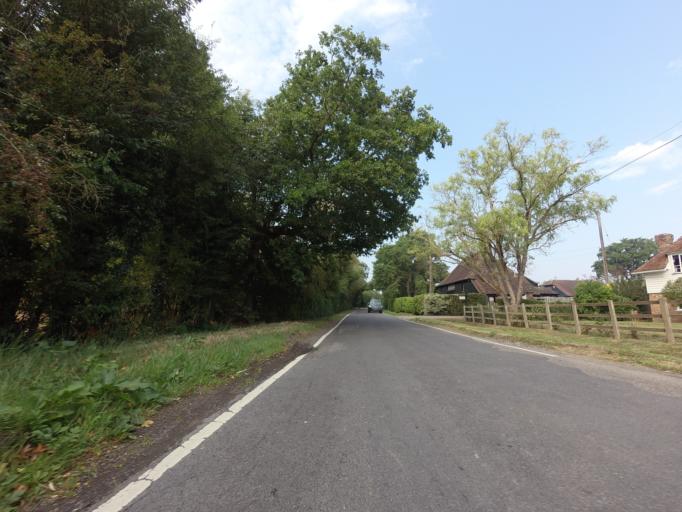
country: GB
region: England
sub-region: Kent
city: Tenterden
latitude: 51.1193
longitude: 0.7073
